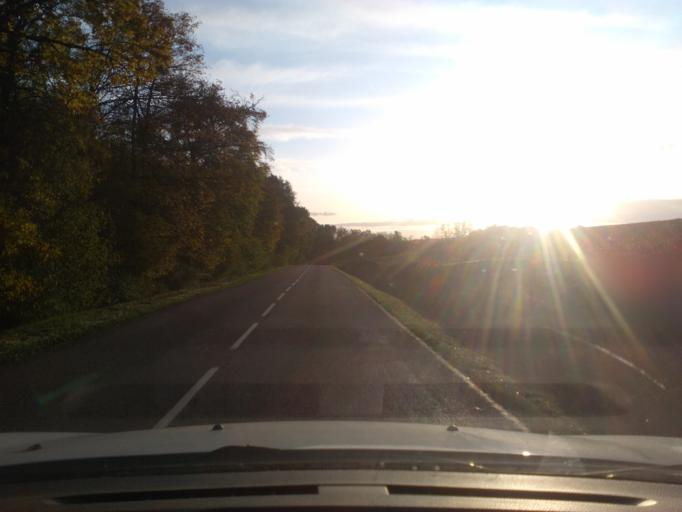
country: FR
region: Lorraine
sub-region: Departement des Vosges
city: Mirecourt
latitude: 48.2172
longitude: 6.1564
